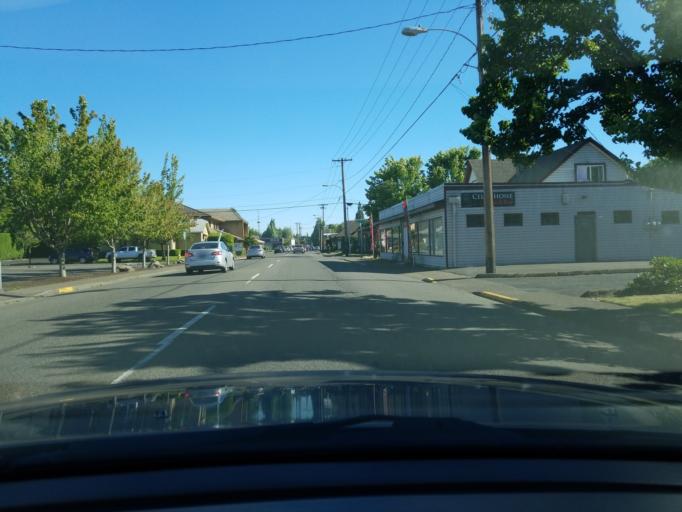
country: US
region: Oregon
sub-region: Yamhill County
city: McMinnville
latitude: 45.2141
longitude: -123.1990
